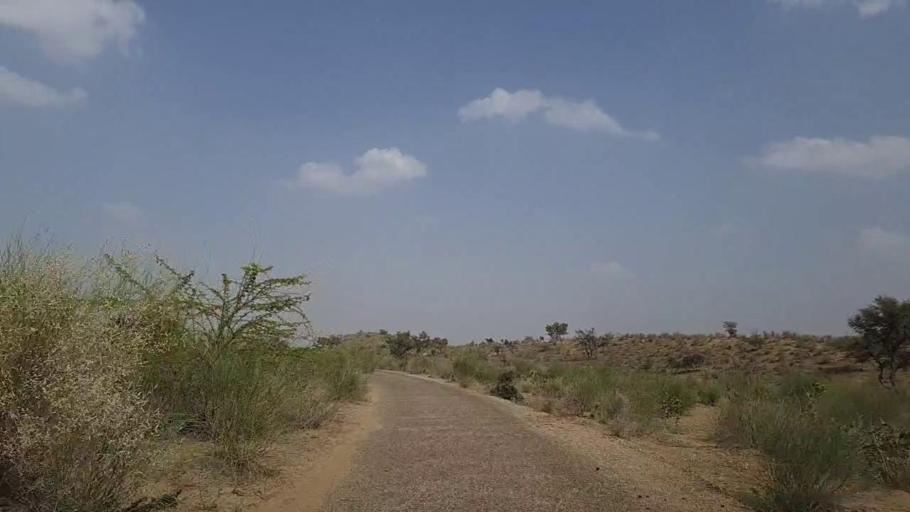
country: PK
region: Sindh
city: Islamkot
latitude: 24.7885
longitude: 70.1045
